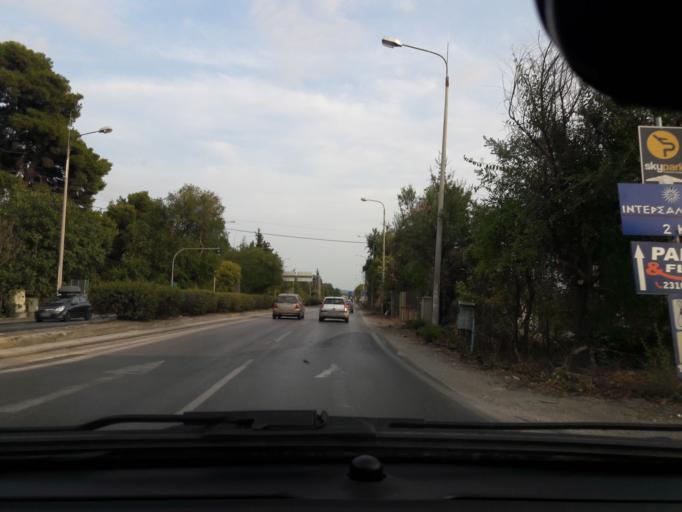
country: GR
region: Central Macedonia
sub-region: Nomos Thessalonikis
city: Thermi
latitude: 40.5381
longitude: 22.9913
